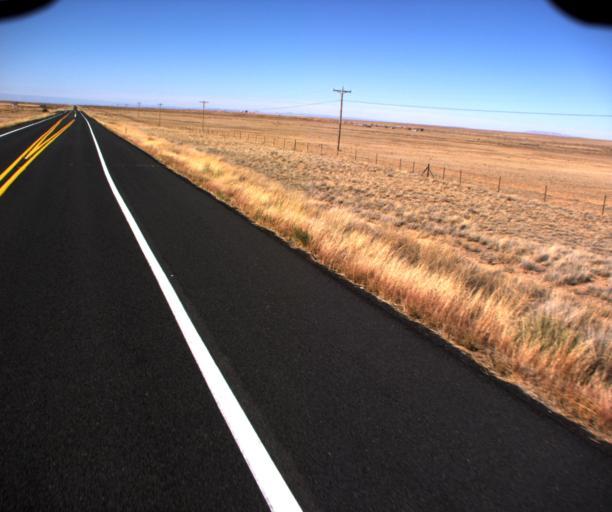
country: US
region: Arizona
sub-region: Coconino County
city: Tuba City
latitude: 35.9963
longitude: -111.0264
